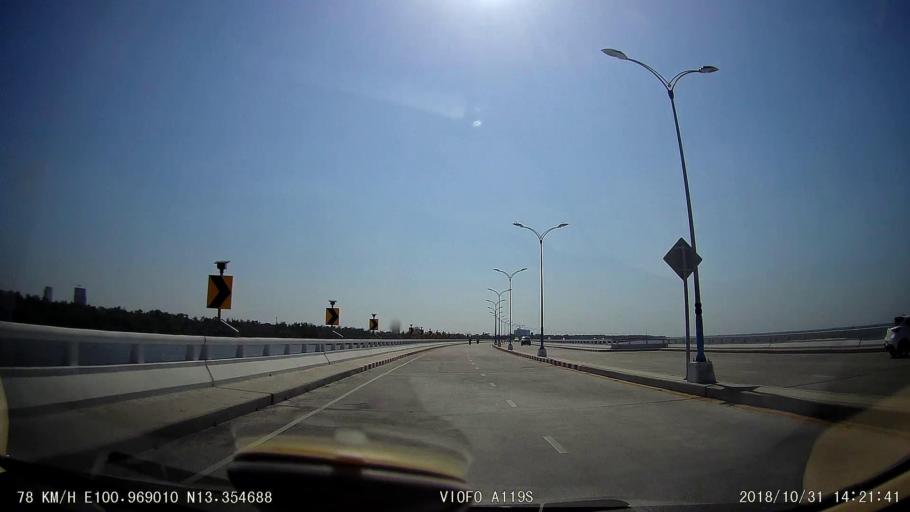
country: TH
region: Chon Buri
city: Chon Buri
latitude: 13.3540
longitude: 100.9683
